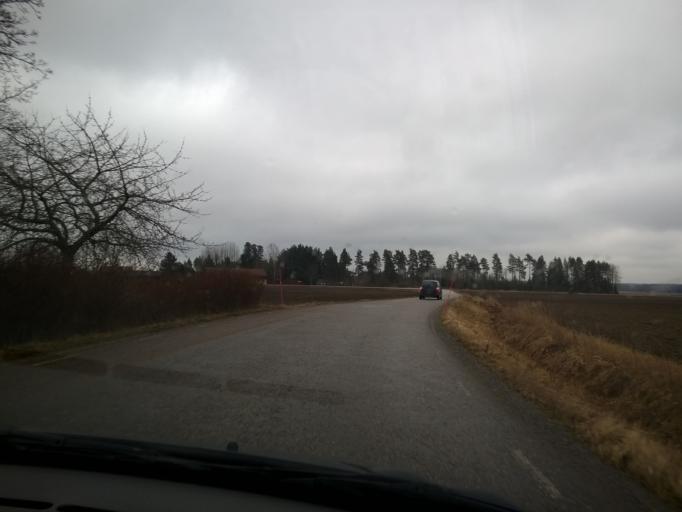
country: SE
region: Uppsala
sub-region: Osthammars Kommun
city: Bjorklinge
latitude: 60.1615
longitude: 17.5283
